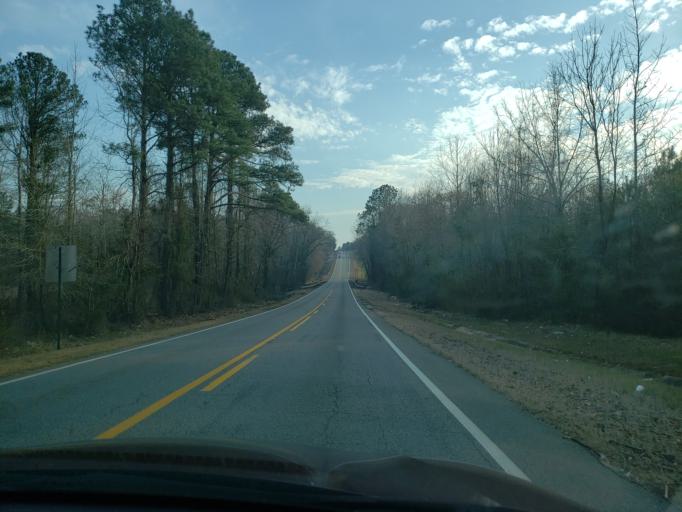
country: US
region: Alabama
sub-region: Hale County
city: Moundville
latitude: 32.9255
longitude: -87.6369
